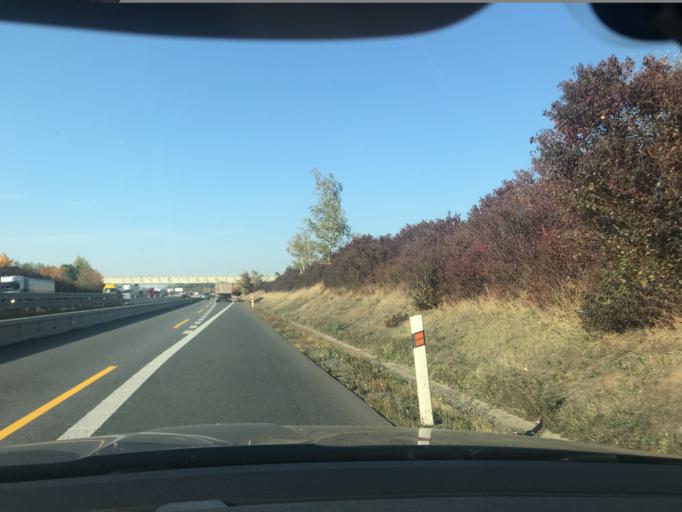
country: CZ
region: Central Bohemia
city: Zdiby
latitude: 50.2029
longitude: 14.4380
